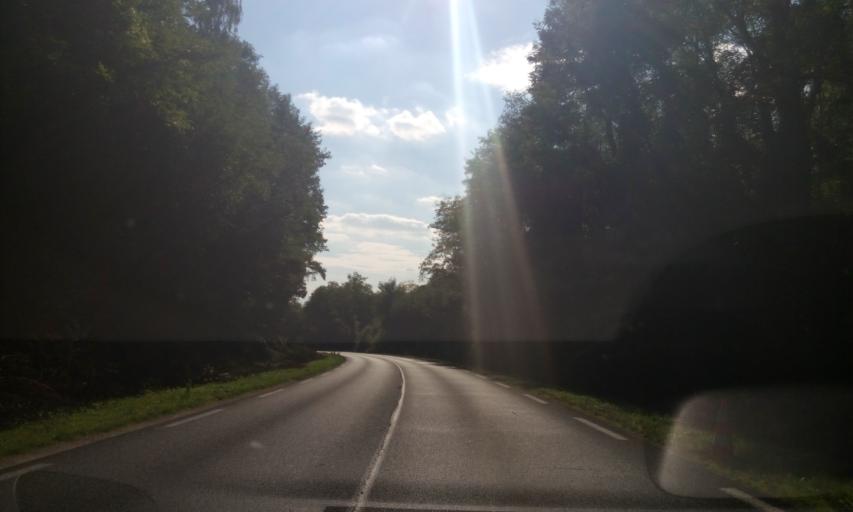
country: FR
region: Centre
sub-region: Departement d'Indre-et-Loire
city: Poce-sur-Cisse
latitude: 47.4502
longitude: 1.0083
